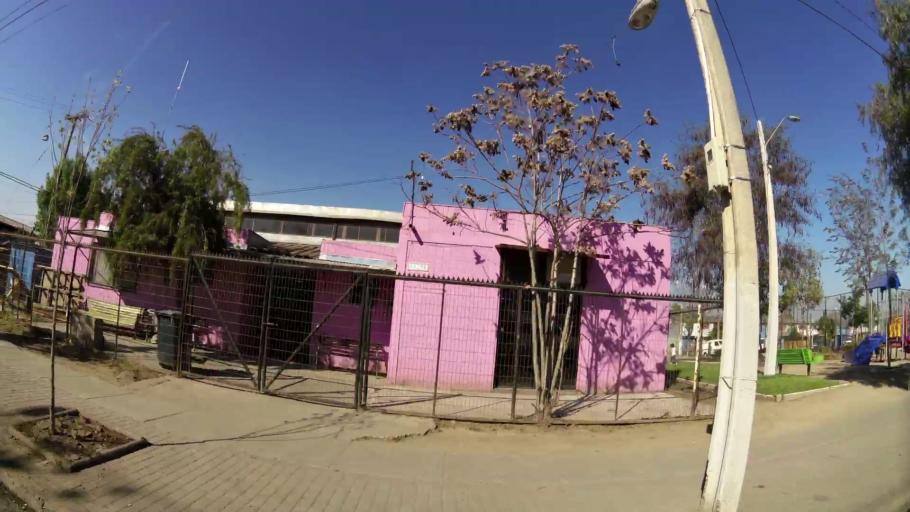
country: CL
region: Santiago Metropolitan
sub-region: Provincia de Santiago
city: La Pintana
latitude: -33.5656
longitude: -70.6098
